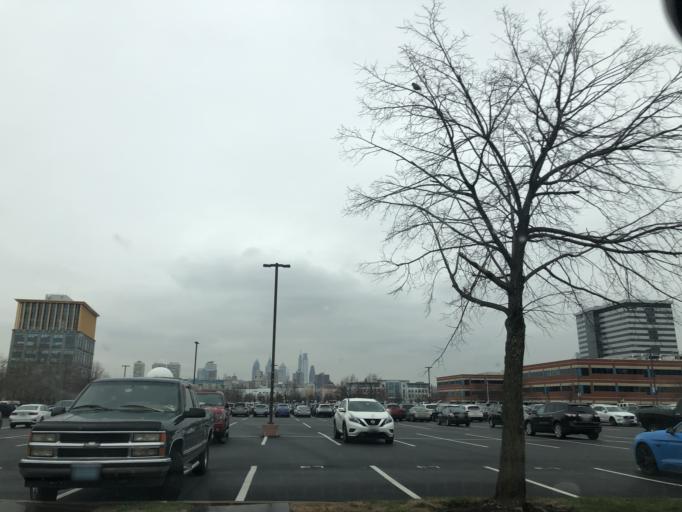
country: US
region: New Jersey
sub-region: Camden County
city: Camden
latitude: 39.9447
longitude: -75.1256
